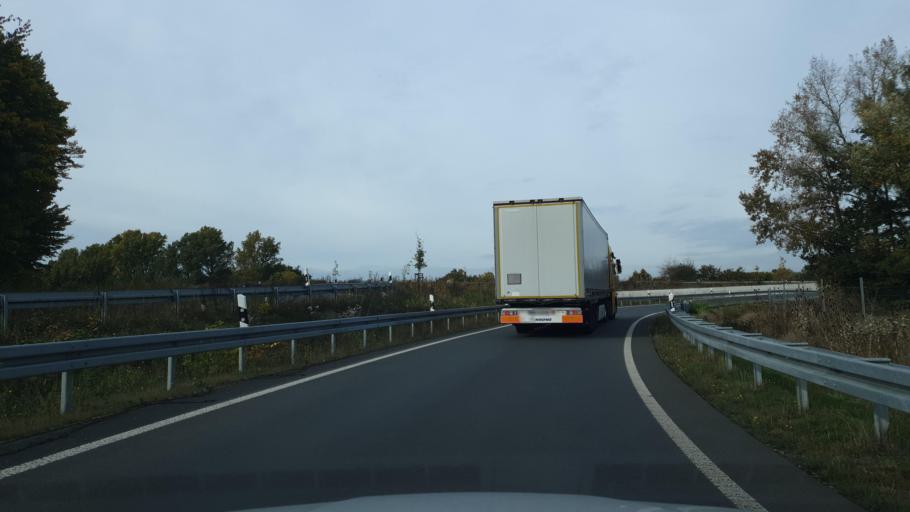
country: DE
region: North Rhine-Westphalia
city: Bad Oeynhausen
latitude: 52.2028
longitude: 8.7480
